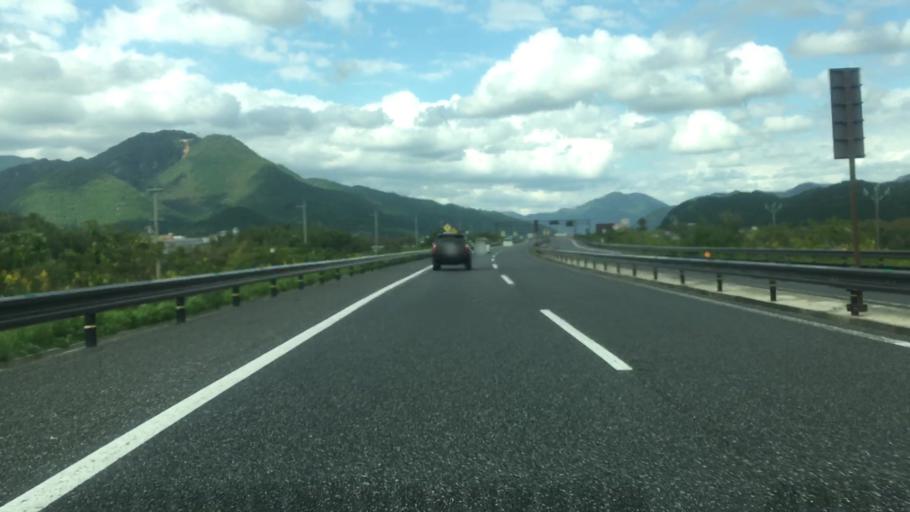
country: JP
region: Kyoto
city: Fukuchiyama
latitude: 35.1666
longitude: 135.0438
